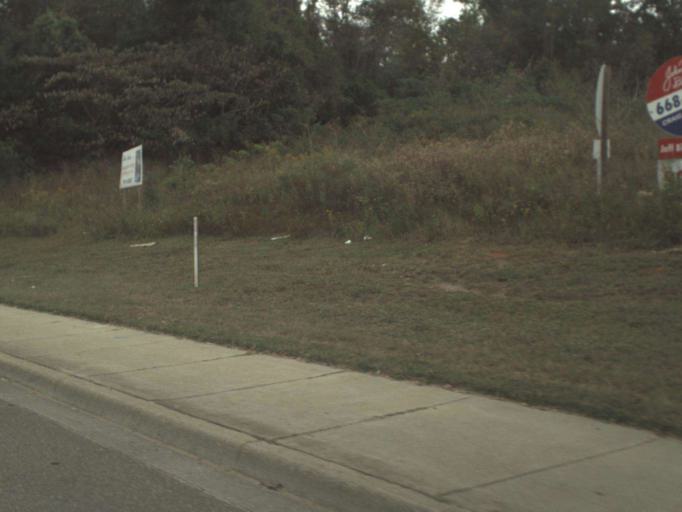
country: US
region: Florida
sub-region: Leon County
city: Tallahassee
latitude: 30.4678
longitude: -84.2303
